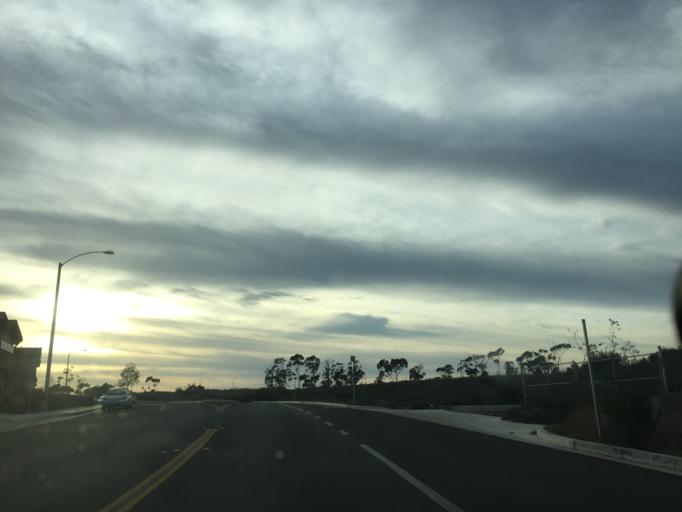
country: US
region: California
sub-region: Santa Barbara County
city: Goleta
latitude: 34.4358
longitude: -119.8496
